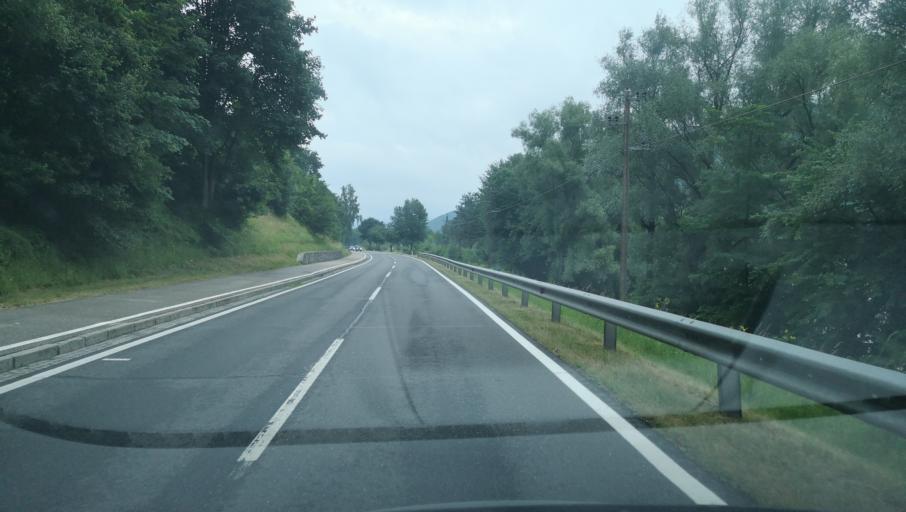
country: AT
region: Lower Austria
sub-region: Politischer Bezirk Krems
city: Aggsbach
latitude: 48.3059
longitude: 15.4071
